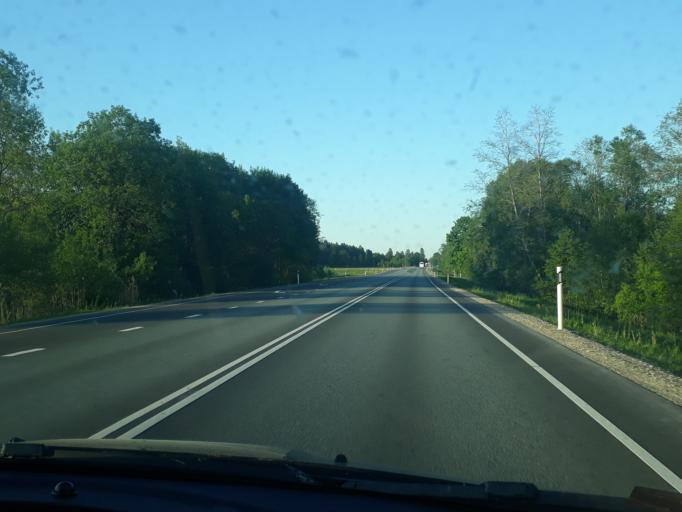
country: EE
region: Paernumaa
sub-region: Tootsi vald
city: Tootsi
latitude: 58.4912
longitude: 24.7585
